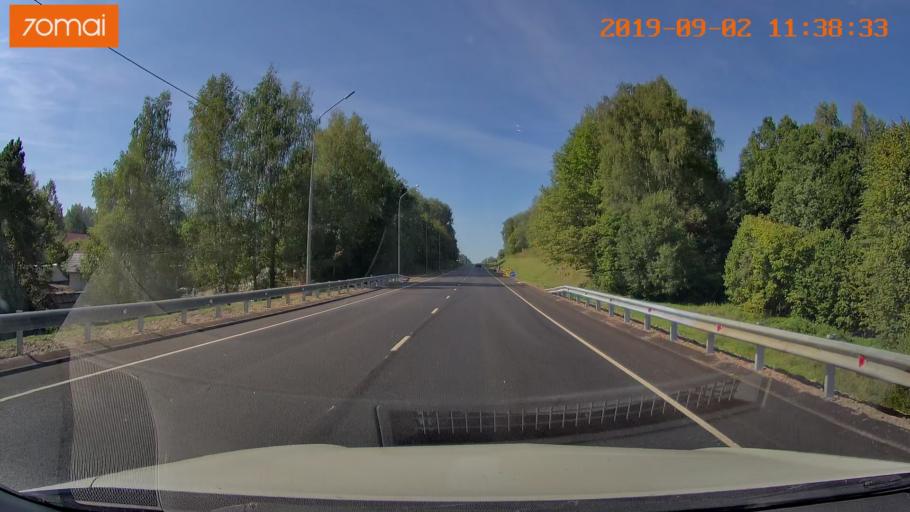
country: RU
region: Smolensk
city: Oster
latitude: 53.9126
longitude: 32.7384
